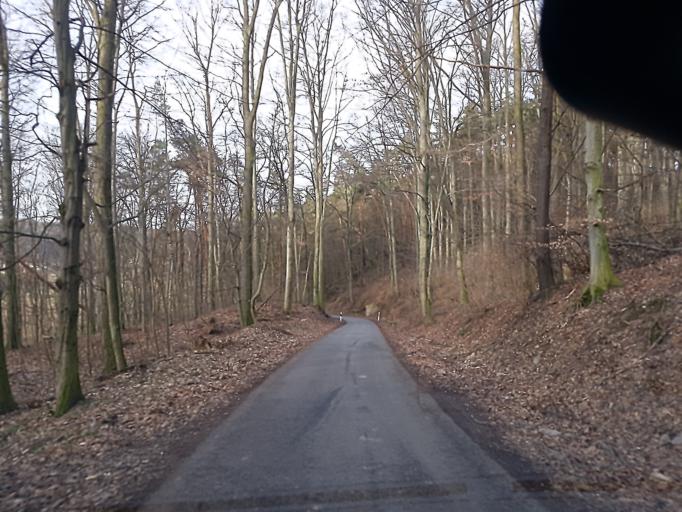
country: DE
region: Saxony
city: Bockelwitz
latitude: 51.1611
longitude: 12.9922
